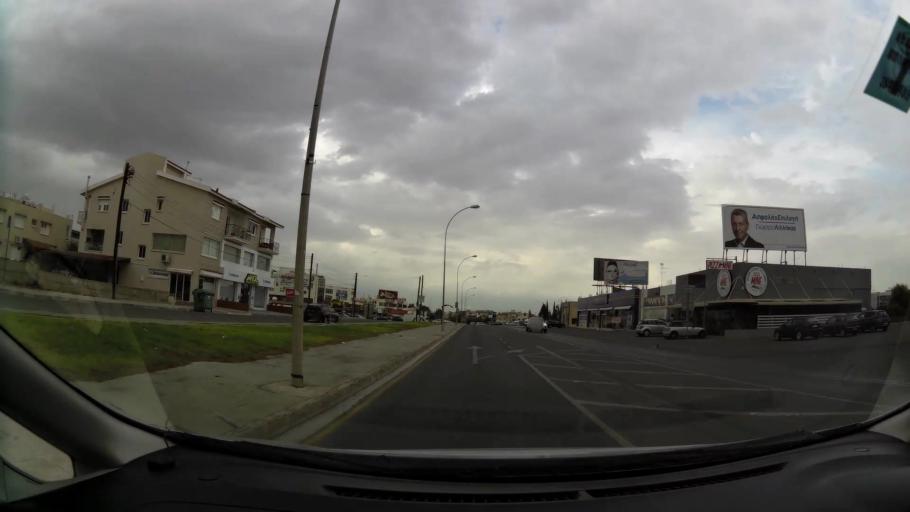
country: CY
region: Lefkosia
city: Nicosia
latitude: 35.1333
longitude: 33.3578
